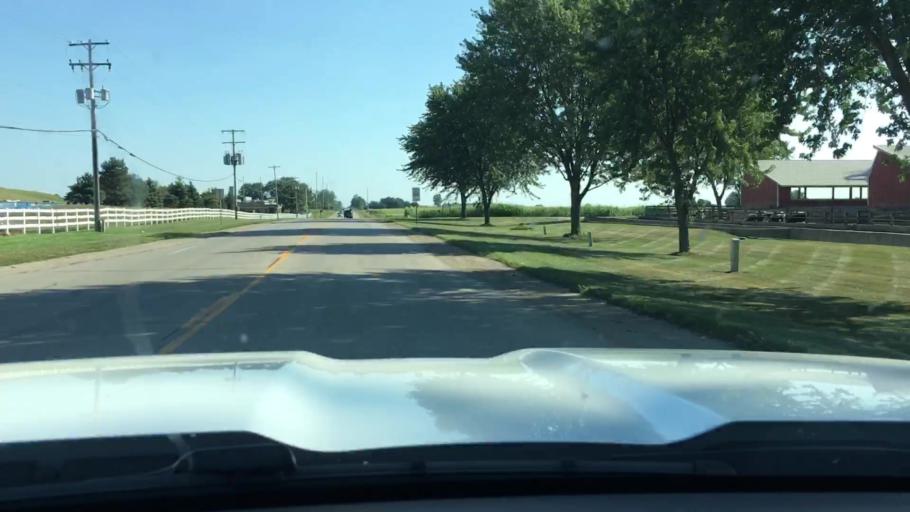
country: US
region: Michigan
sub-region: Ottawa County
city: Coopersville
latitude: 43.0517
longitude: -85.9568
